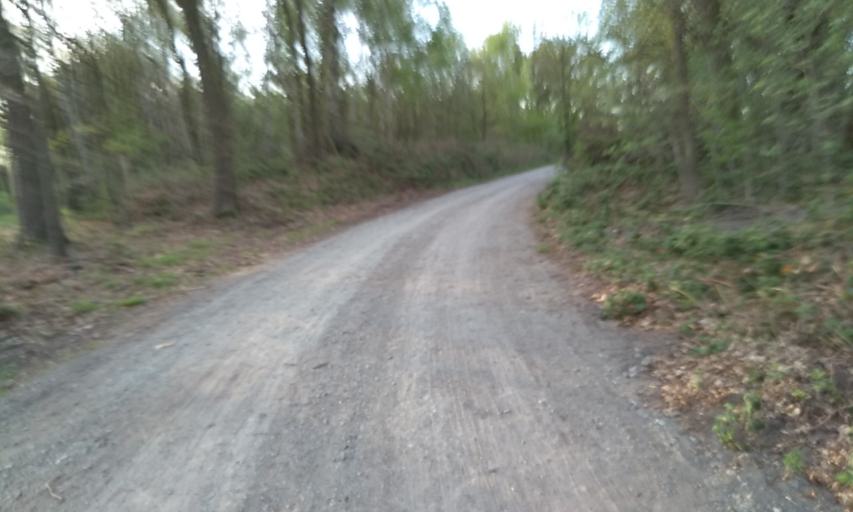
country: DE
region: Lower Saxony
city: Nottensdorf
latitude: 53.4895
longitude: 9.6195
